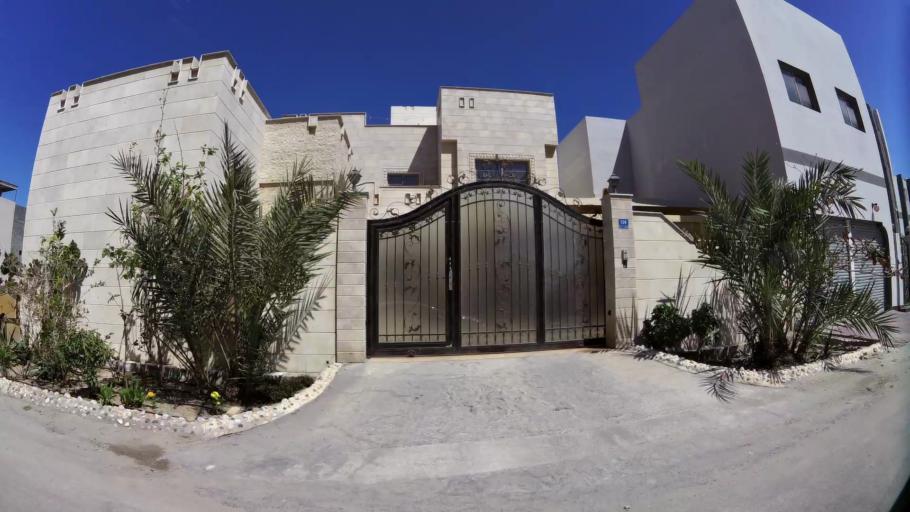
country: BH
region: Muharraq
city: Al Muharraq
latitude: 26.2775
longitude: 50.6376
